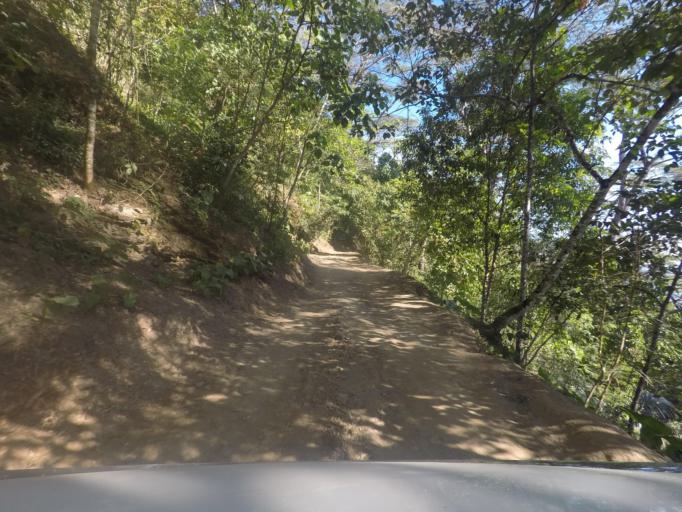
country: TL
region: Ermera
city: Gleno
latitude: -8.7464
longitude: 125.3517
